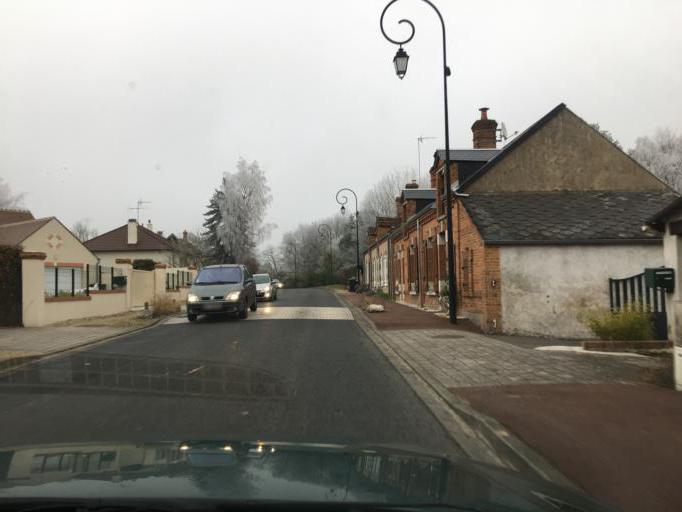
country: FR
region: Centre
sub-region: Departement du Loiret
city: Ligny-le-Ribault
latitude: 47.6850
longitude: 1.7827
